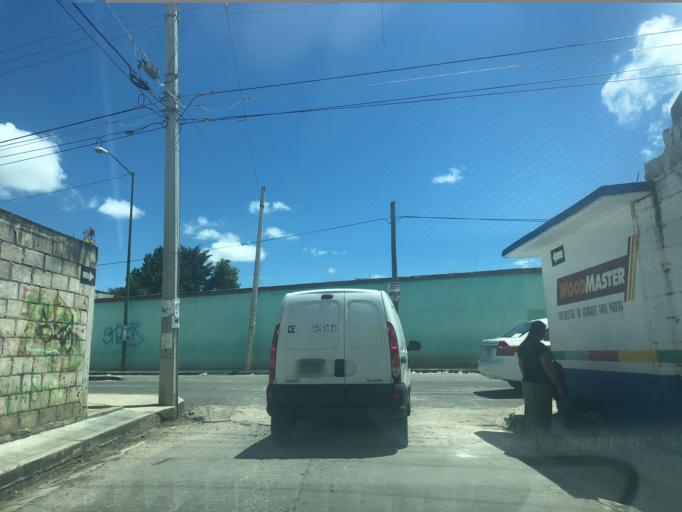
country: MX
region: Chiapas
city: San Cristobal de las Casas
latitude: 16.7173
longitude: -92.6407
